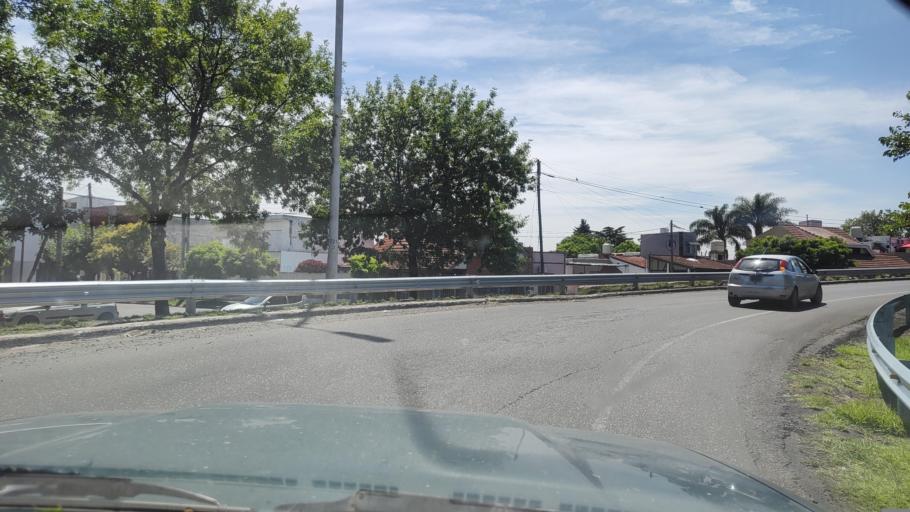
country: AR
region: Buenos Aires
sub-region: Partido de Moron
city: Moron
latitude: -34.6315
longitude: -58.6291
